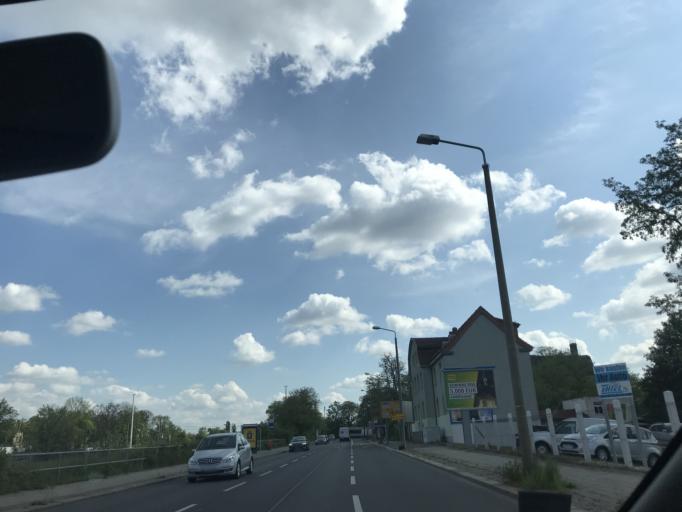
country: DE
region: Saxony
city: Leipzig
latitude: 51.3521
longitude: 12.3006
